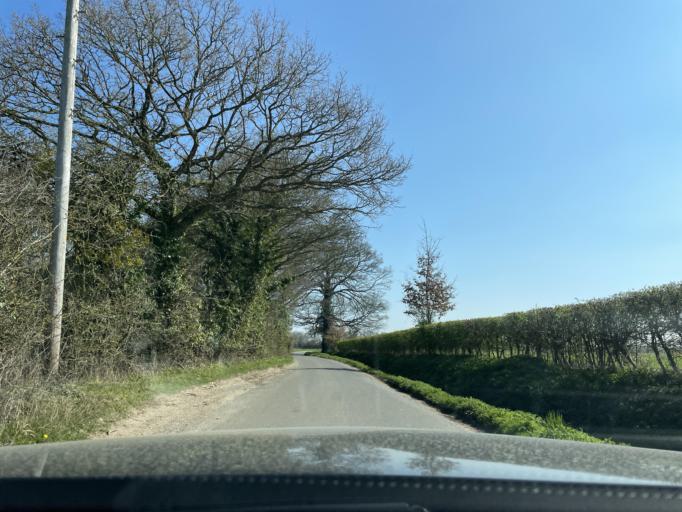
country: GB
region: England
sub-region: Norfolk
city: Hingham
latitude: 52.6181
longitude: 0.9895
